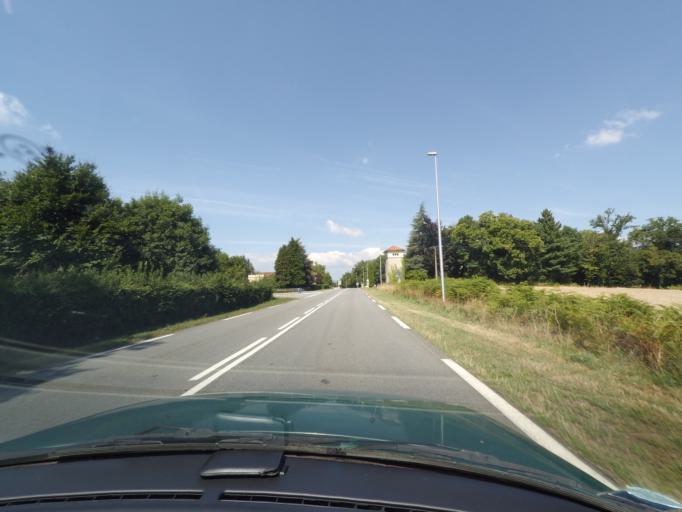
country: FR
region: Limousin
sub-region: Departement de la Haute-Vienne
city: Feytiat
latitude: 45.7993
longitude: 1.3872
